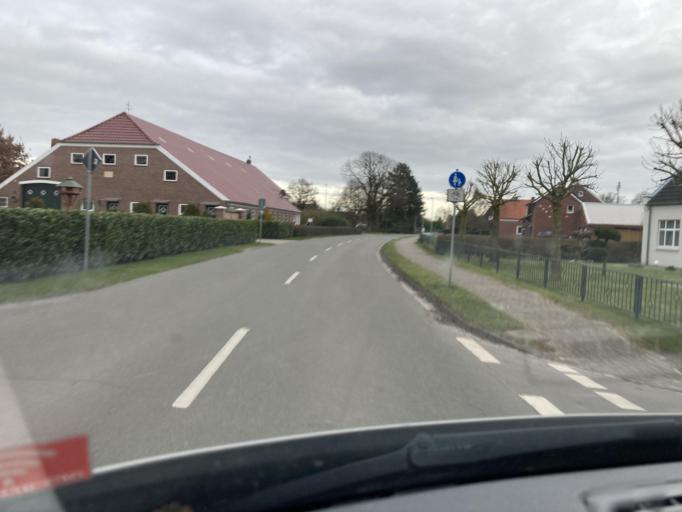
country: DE
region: Lower Saxony
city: Leer
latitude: 53.1670
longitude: 7.4458
